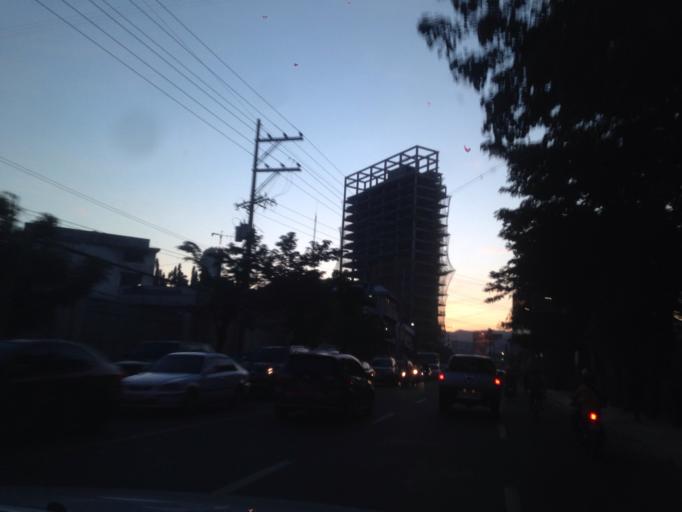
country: PH
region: Central Visayas
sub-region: Cebu City
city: Baugo
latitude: 10.3095
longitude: 123.9060
